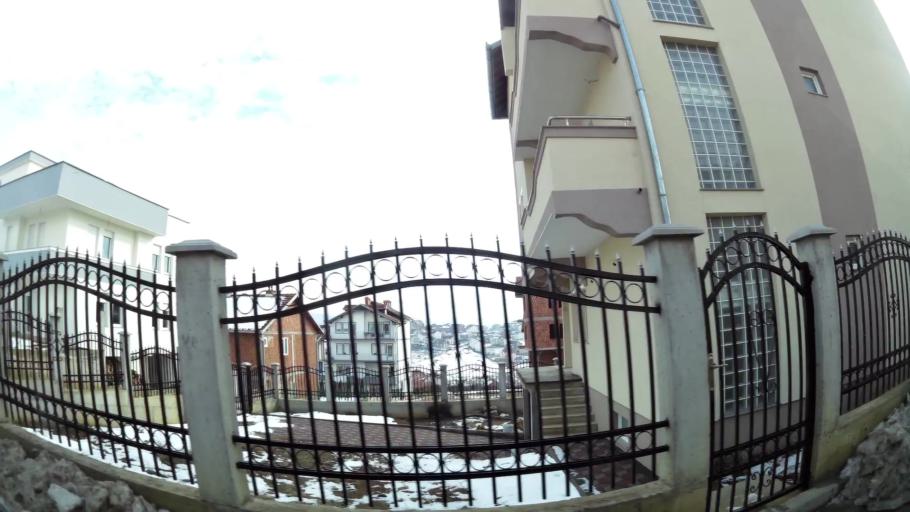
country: XK
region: Pristina
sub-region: Komuna e Prishtines
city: Pristina
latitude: 42.6824
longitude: 21.1533
